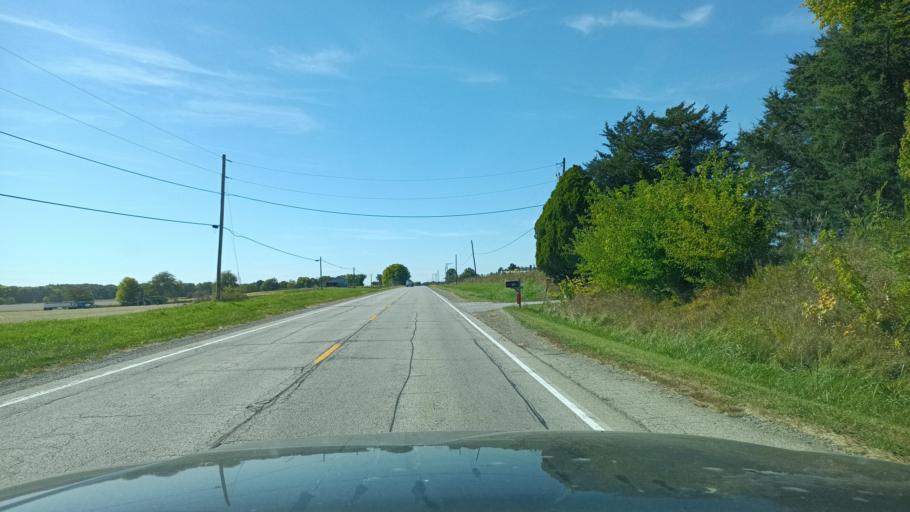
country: US
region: Illinois
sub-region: De Witt County
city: Farmer City
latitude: 40.2322
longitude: -88.6662
